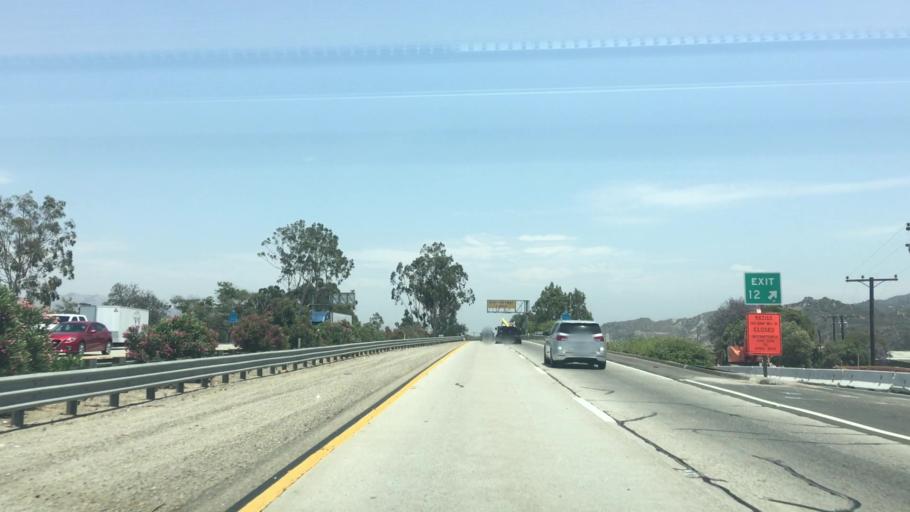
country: US
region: California
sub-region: Ventura County
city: Santa Paula
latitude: 34.3496
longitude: -119.0599
